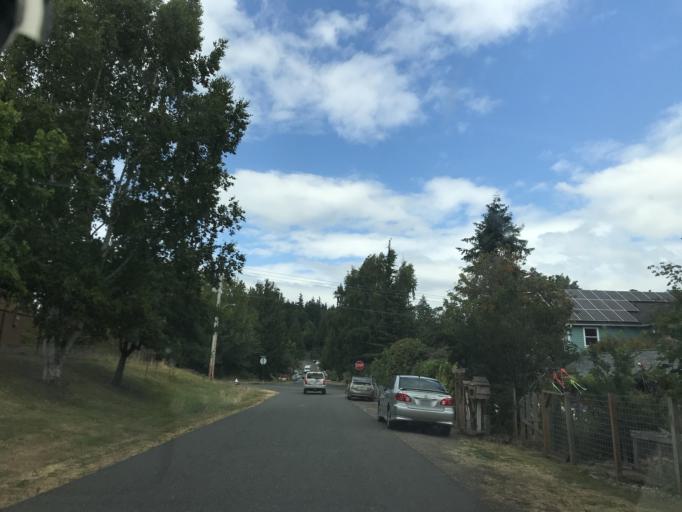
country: US
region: Washington
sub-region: Whatcom County
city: Bellingham
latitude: 48.7188
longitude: -122.4931
